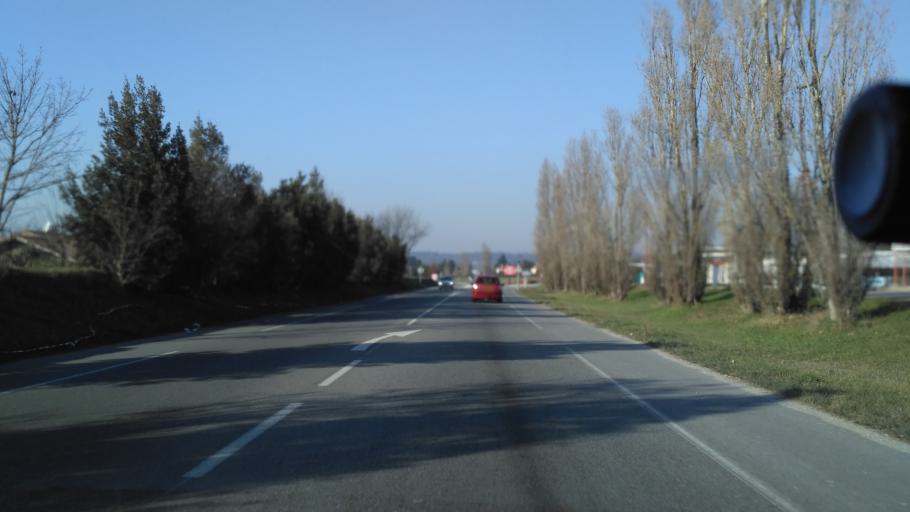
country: FR
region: Rhone-Alpes
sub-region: Departement de la Drome
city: Mours-Saint-Eusebe
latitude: 45.0586
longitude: 5.0609
